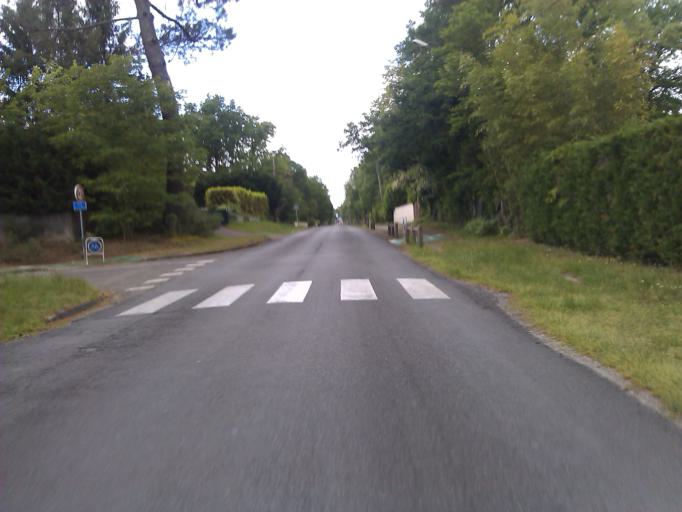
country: FR
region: Aquitaine
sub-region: Departement de la Gironde
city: Cestas
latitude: 44.7428
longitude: -0.6899
